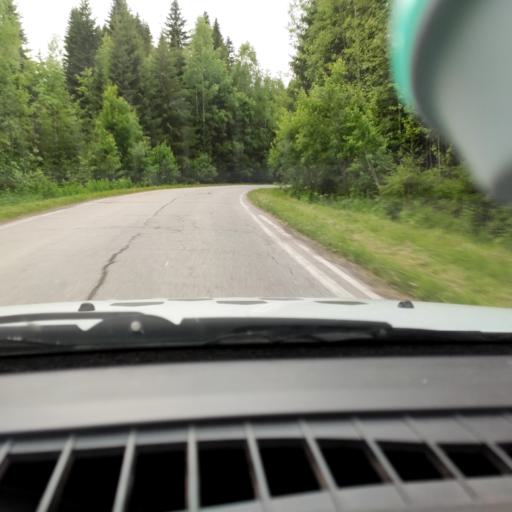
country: RU
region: Perm
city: Lys'va
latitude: 58.1153
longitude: 57.6992
